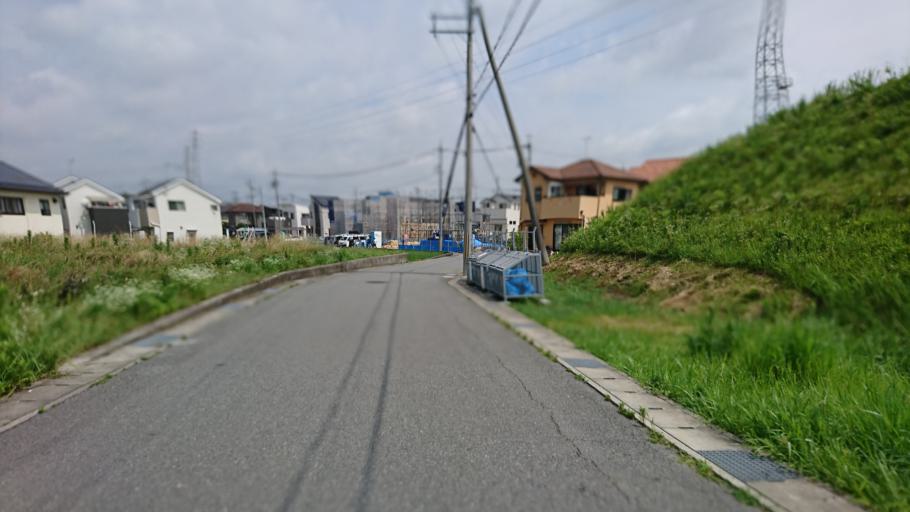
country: JP
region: Hyogo
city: Miki
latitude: 34.7520
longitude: 134.9163
